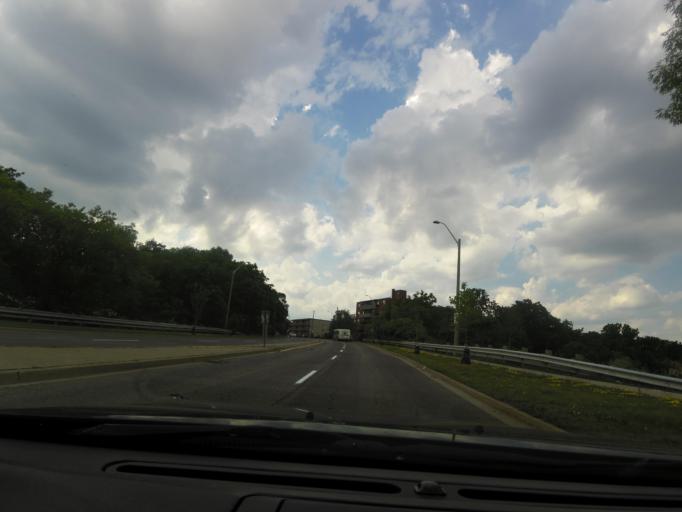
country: CA
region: Ontario
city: Hamilton
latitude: 43.2282
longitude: -79.7924
